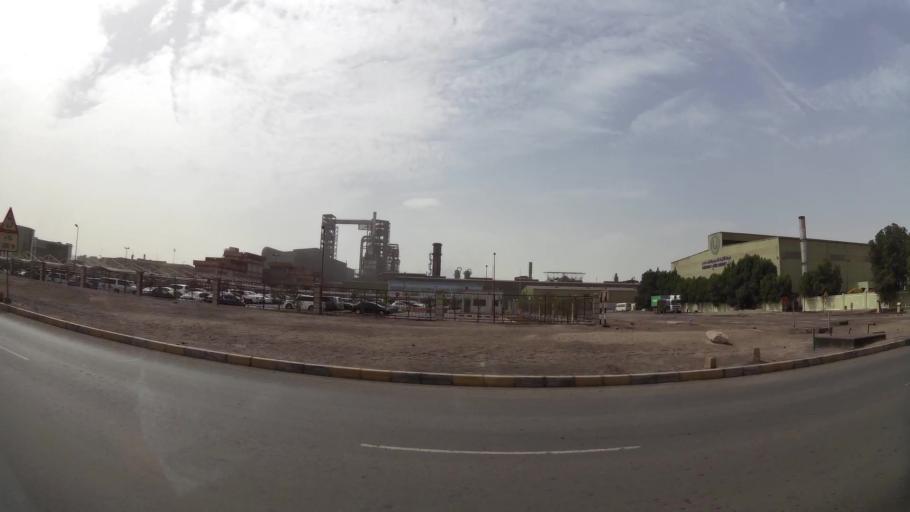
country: AE
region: Abu Dhabi
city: Abu Dhabi
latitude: 24.3249
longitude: 54.4737
